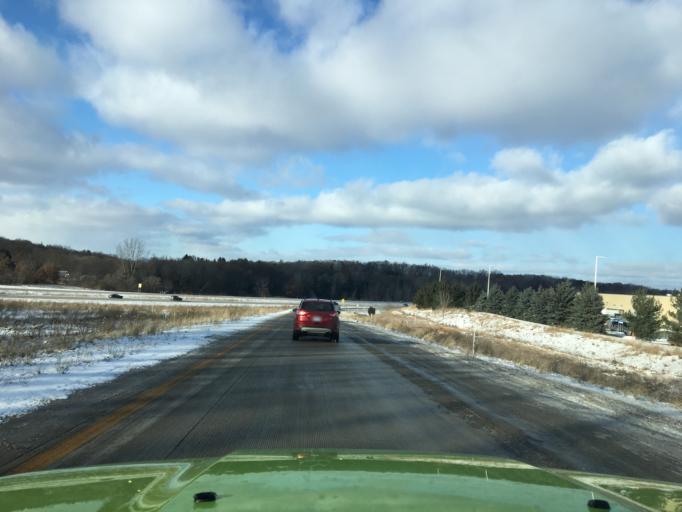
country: US
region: Michigan
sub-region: Kent County
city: Rockford
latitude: 43.1183
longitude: -85.6039
